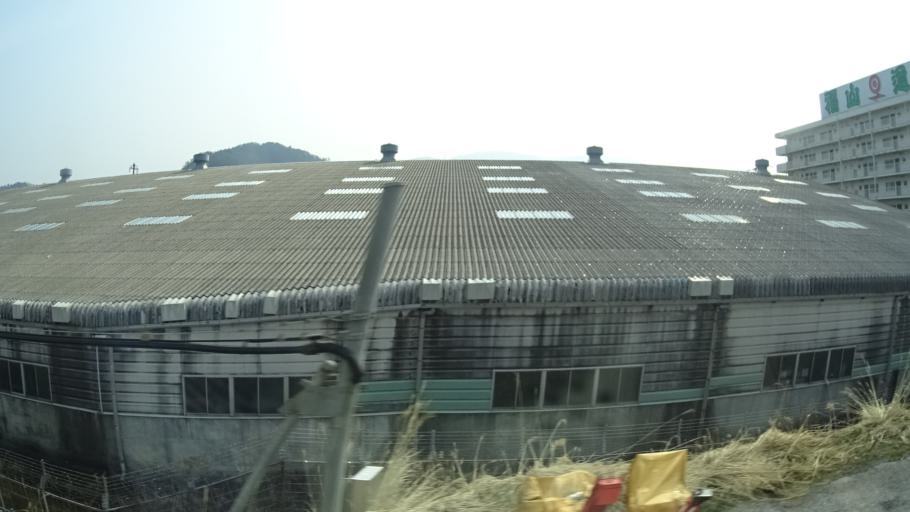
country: JP
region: Shiga Prefecture
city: Hikone
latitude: 35.2900
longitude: 136.2819
